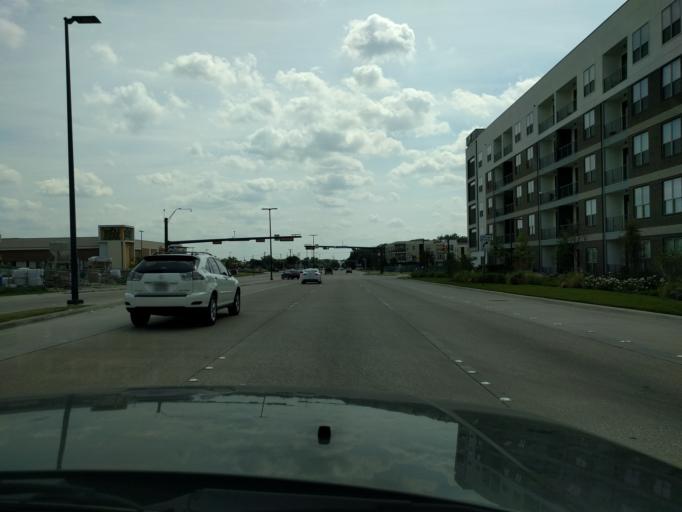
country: US
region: Texas
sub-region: Collin County
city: Plano
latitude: 33.0002
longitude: -96.6995
